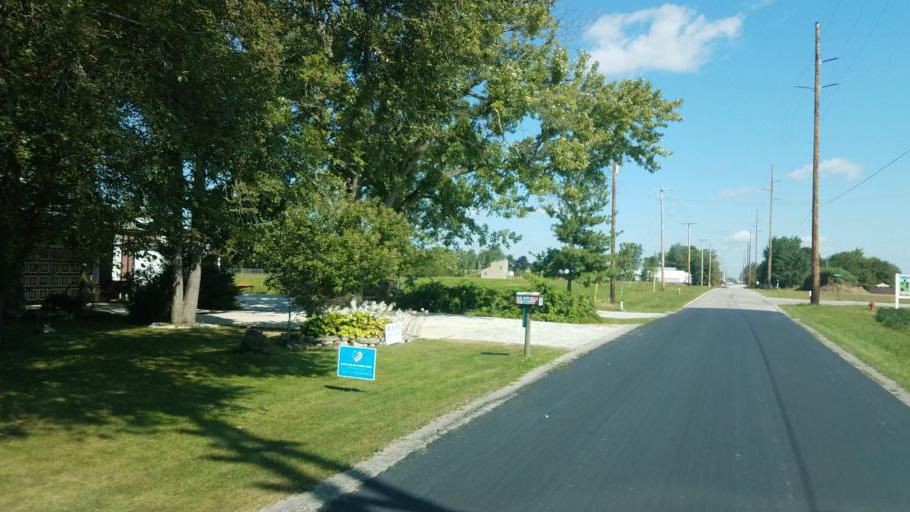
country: US
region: Ohio
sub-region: Wyandot County
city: Carey
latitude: 40.9458
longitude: -83.3675
